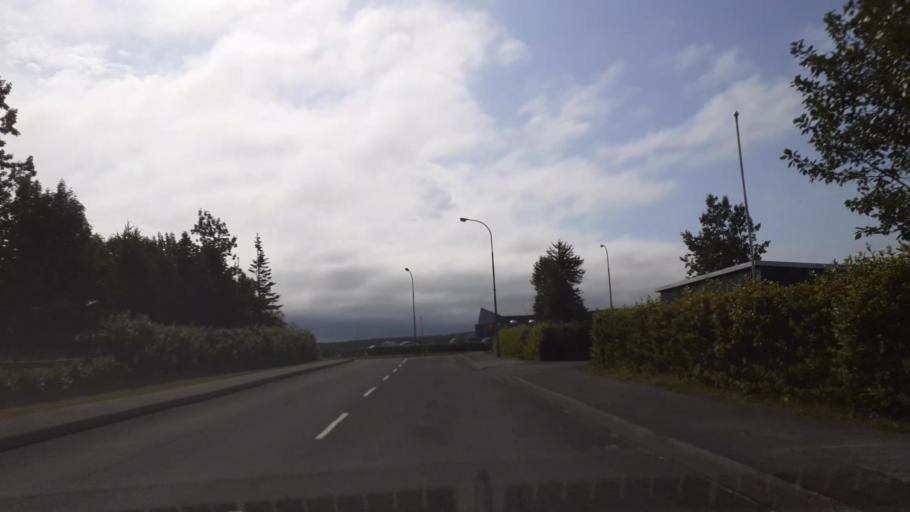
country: IS
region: Northwest
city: Saudarkrokur
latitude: 65.6610
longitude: -20.2800
